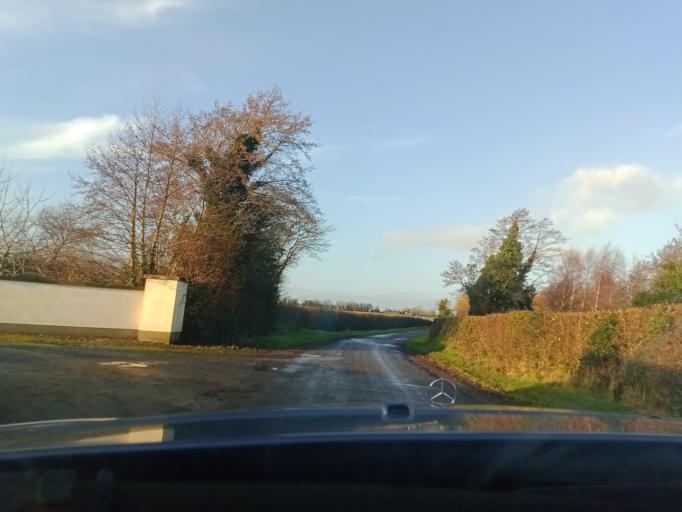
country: IE
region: Leinster
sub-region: Kilkenny
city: Callan
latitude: 52.4773
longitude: -7.4589
